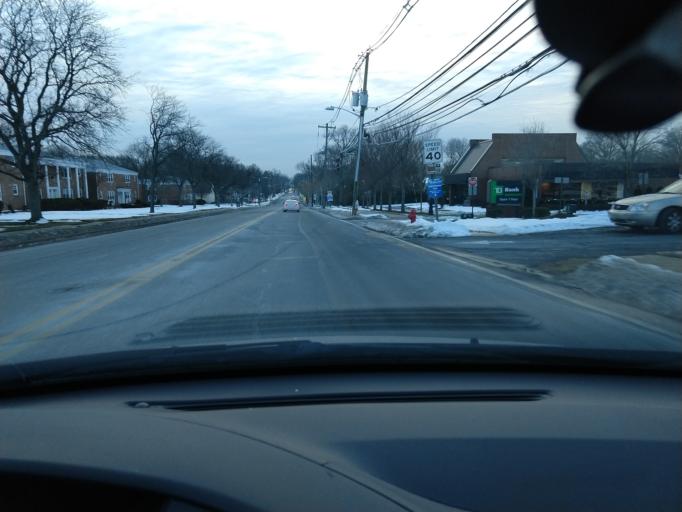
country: US
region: New Jersey
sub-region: Middlesex County
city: Metuchen
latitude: 40.5545
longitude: -74.3473
